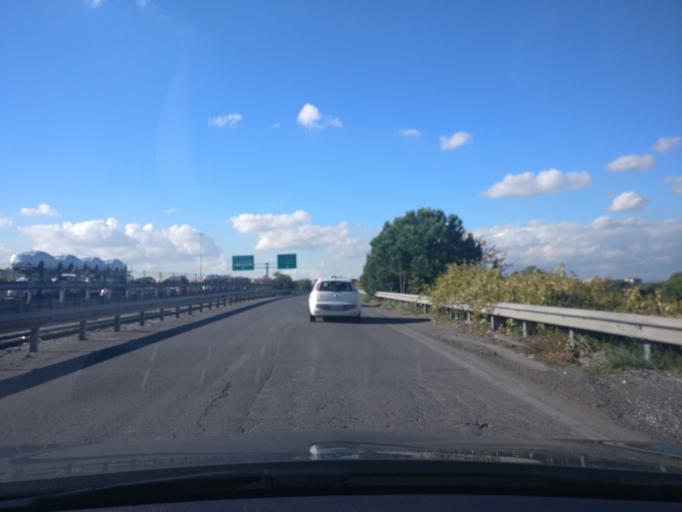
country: IT
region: Latium
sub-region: Citta metropolitana di Roma Capitale
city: Ciampino
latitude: 41.8513
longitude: 12.6032
